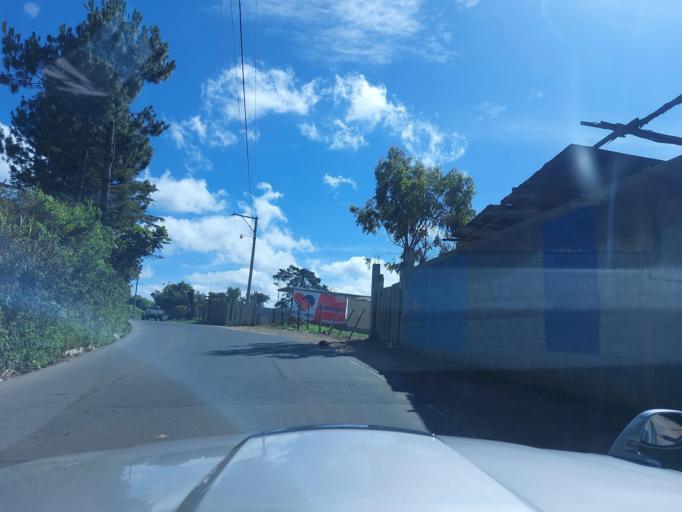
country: GT
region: Chimaltenango
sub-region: Municipio de Zaragoza
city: Zaragoza
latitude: 14.6469
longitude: -90.8976
